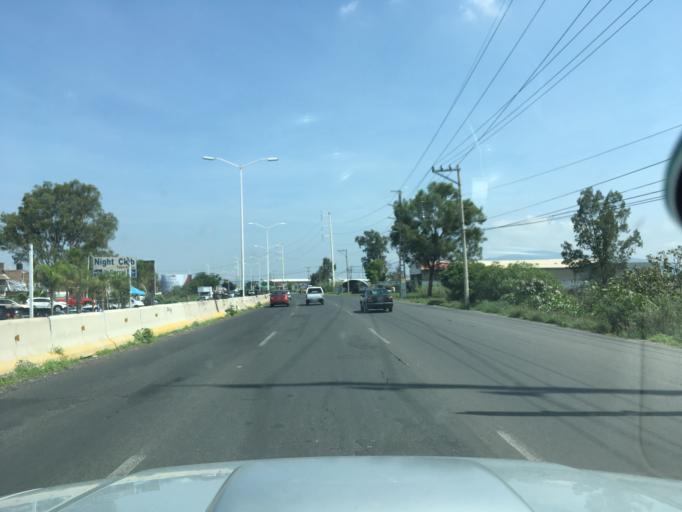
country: MX
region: Jalisco
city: Tonala
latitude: 20.6738
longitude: -103.2370
